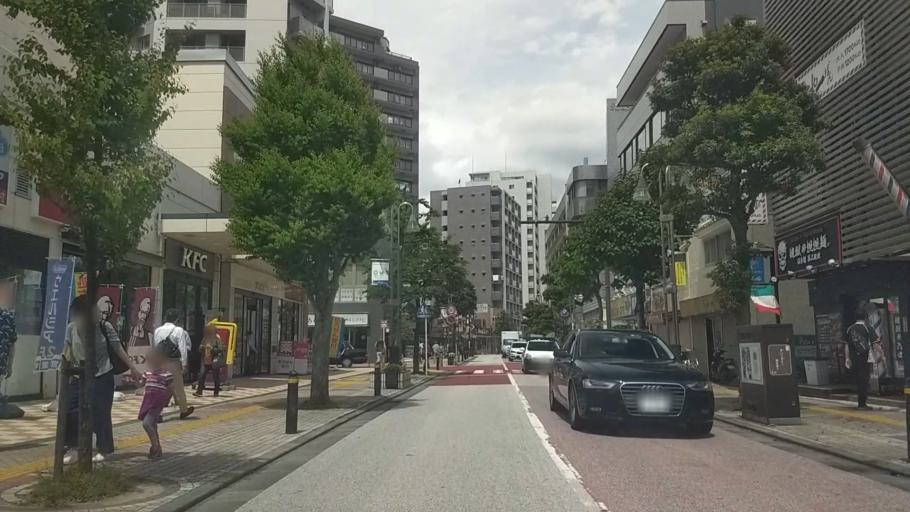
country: JP
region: Kanagawa
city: Fujisawa
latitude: 35.3405
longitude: 139.4850
